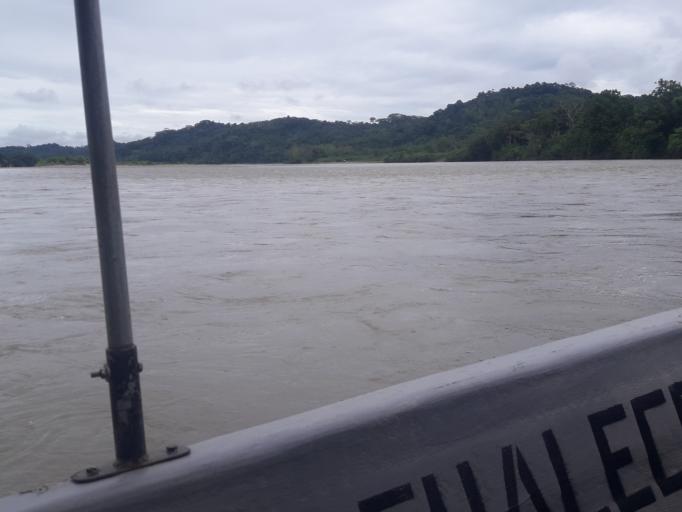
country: EC
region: Orellana
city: Boca Suno
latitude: -0.8797
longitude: -77.2849
